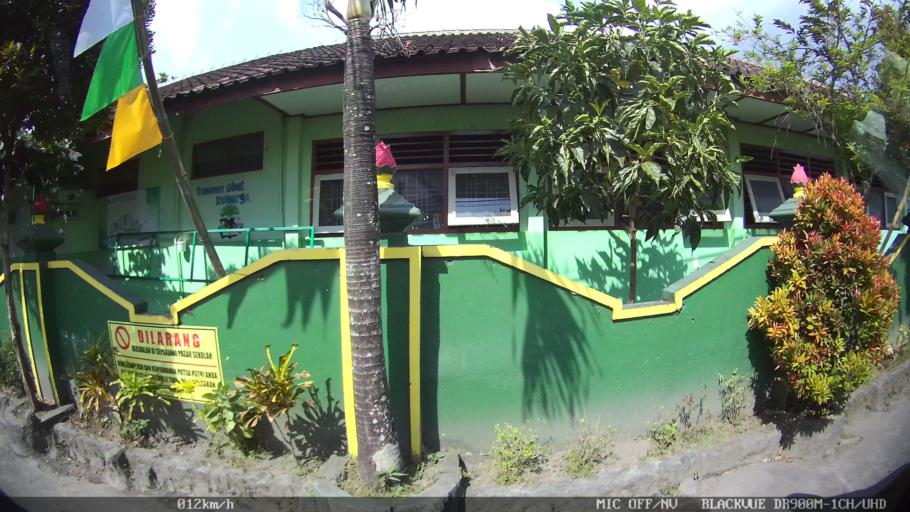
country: ID
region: Daerah Istimewa Yogyakarta
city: Kasihan
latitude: -7.8127
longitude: 110.3282
